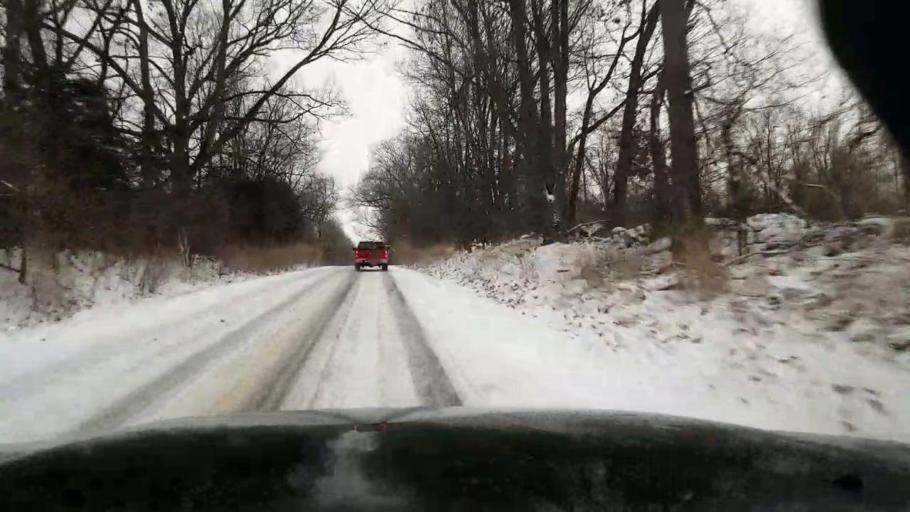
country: US
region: Michigan
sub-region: Jackson County
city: Spring Arbor
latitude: 42.1343
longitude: -84.4986
